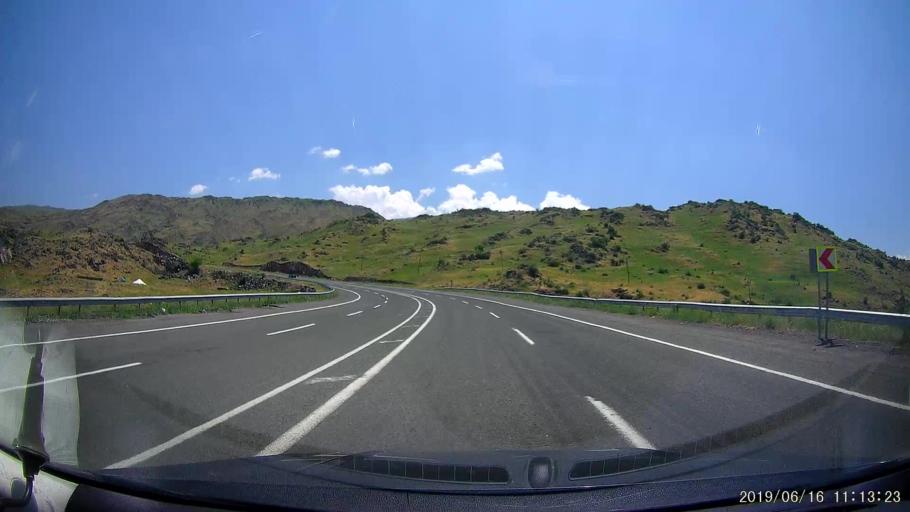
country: TR
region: Igdir
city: Igdir
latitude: 39.7844
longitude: 44.1369
